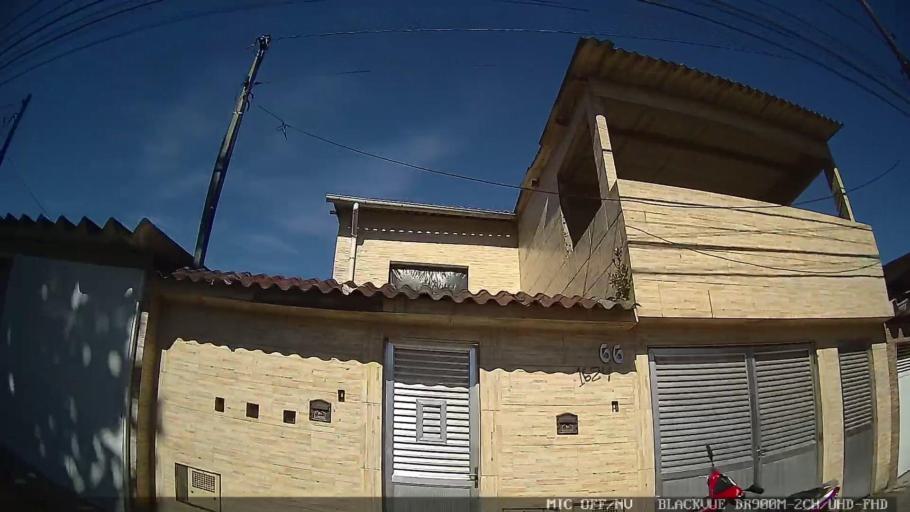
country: BR
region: Sao Paulo
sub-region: Santos
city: Santos
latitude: -23.9486
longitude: -46.2859
